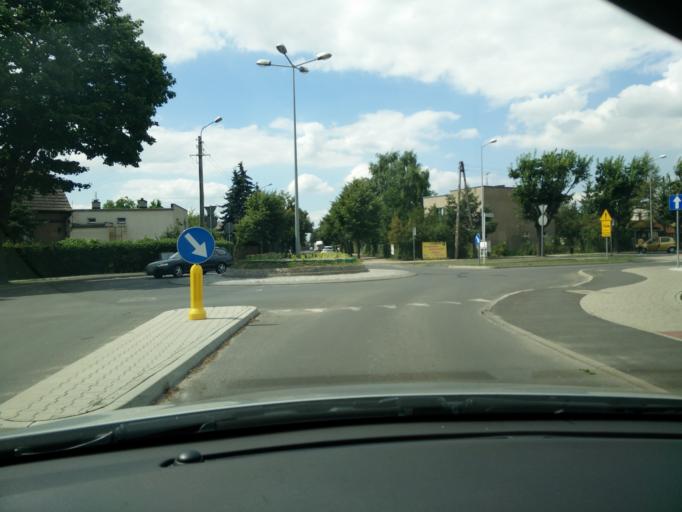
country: PL
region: Greater Poland Voivodeship
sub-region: Powiat sredzki
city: Sroda Wielkopolska
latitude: 52.2291
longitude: 17.2654
